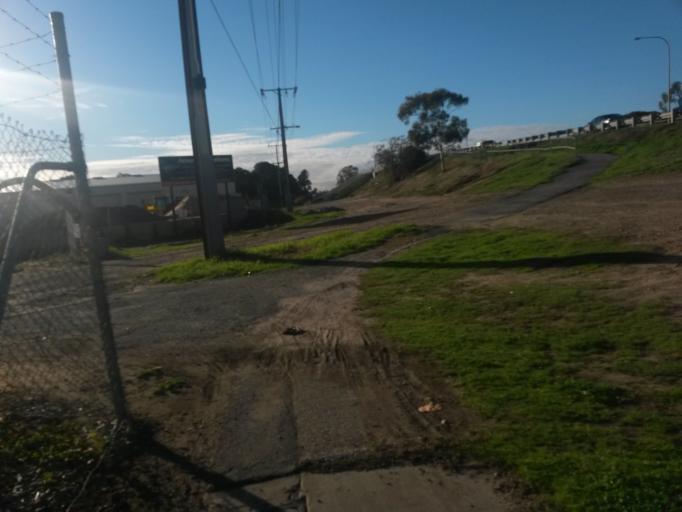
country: AU
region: South Australia
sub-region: Port Adelaide Enfield
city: Alberton
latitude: -34.8520
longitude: 138.5121
